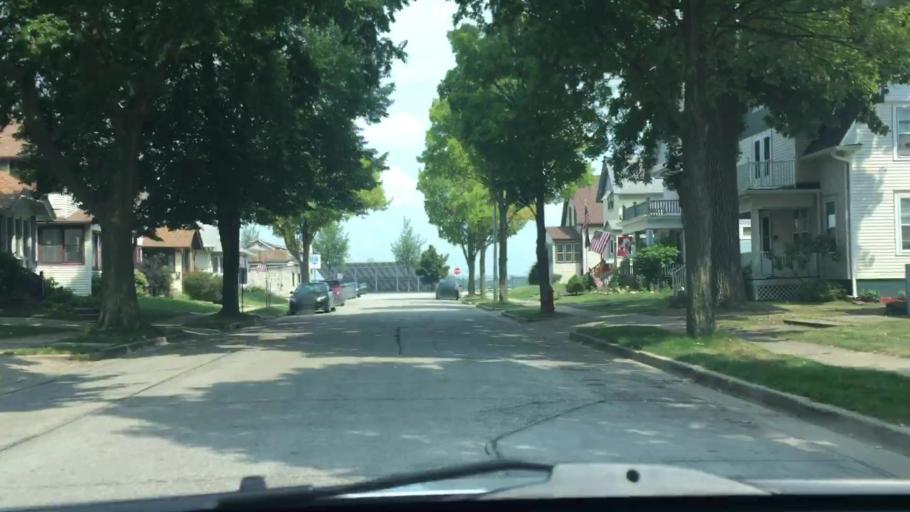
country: US
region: Wisconsin
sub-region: Milwaukee County
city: West Allis
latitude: 43.0156
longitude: -88.0118
